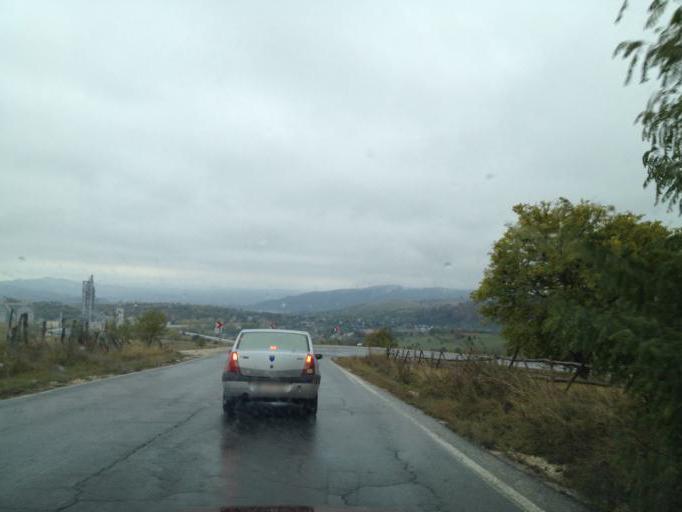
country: RO
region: Arges
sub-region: Comuna Valea Mare-Pravat
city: Valea Mare Pravat
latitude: 45.2949
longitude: 25.1305
